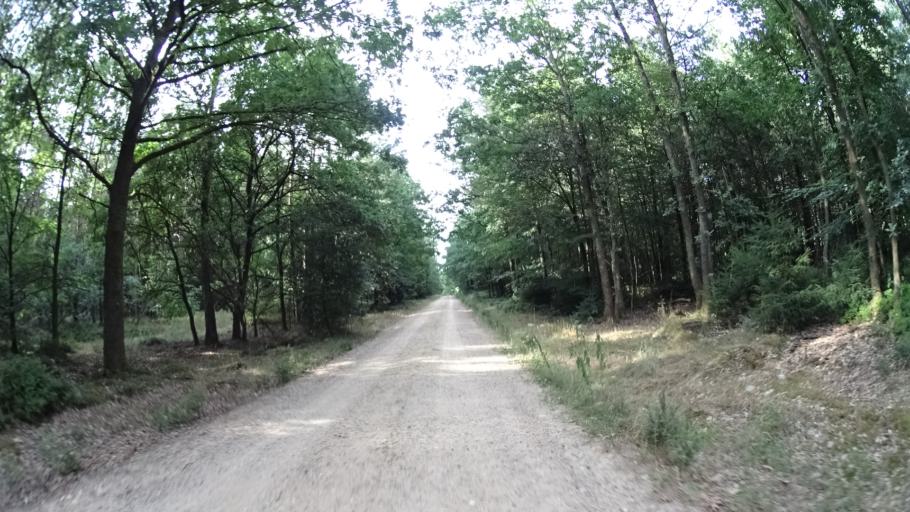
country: DE
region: Lower Saxony
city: Handeloh
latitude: 53.1815
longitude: 9.8843
